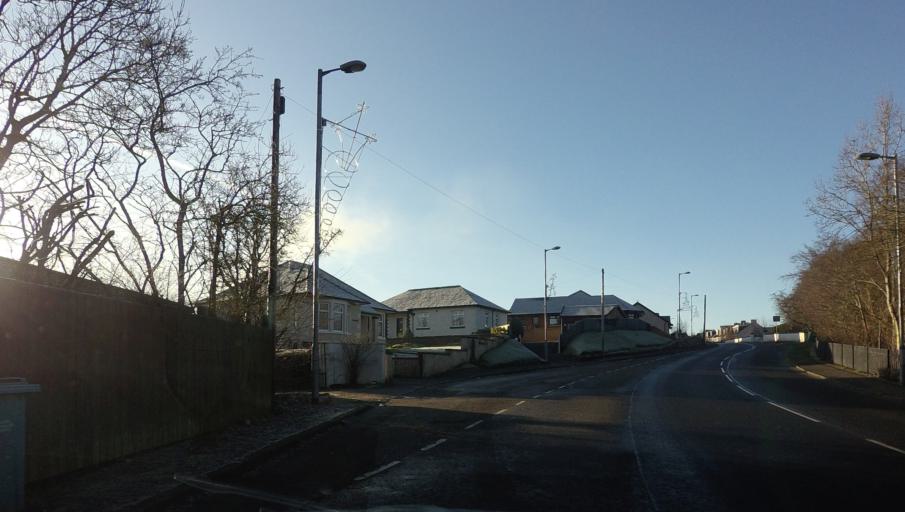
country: GB
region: Scotland
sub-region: North Lanarkshire
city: Newmains
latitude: 55.7894
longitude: -3.8628
